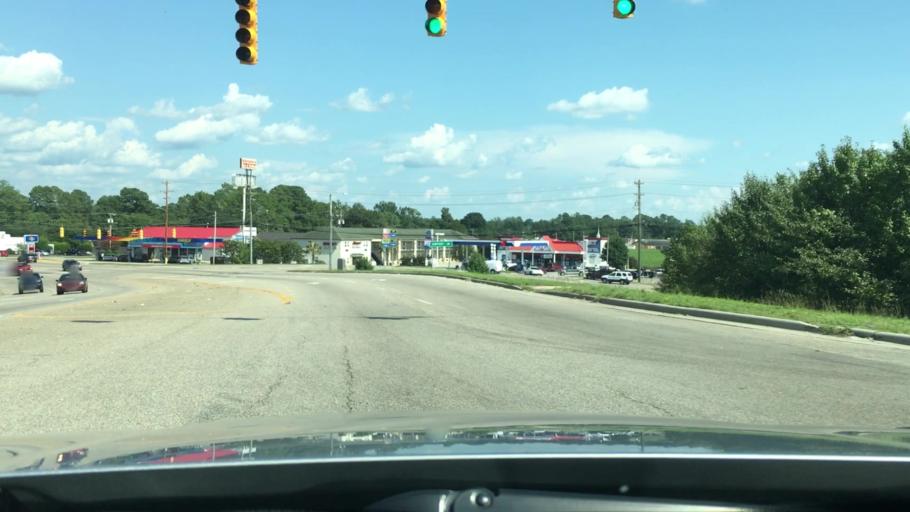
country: US
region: North Carolina
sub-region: Robeson County
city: Lumberton
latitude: 34.6224
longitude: -79.0513
